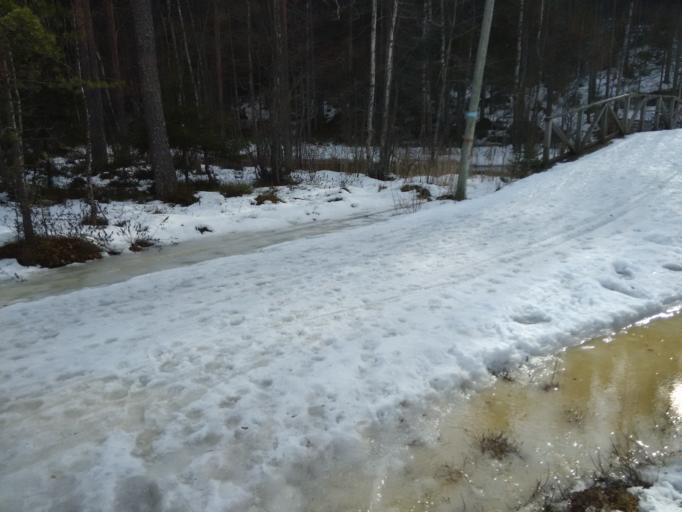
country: FI
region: Pirkanmaa
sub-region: Tampere
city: Tampere
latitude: 61.4385
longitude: 23.8336
